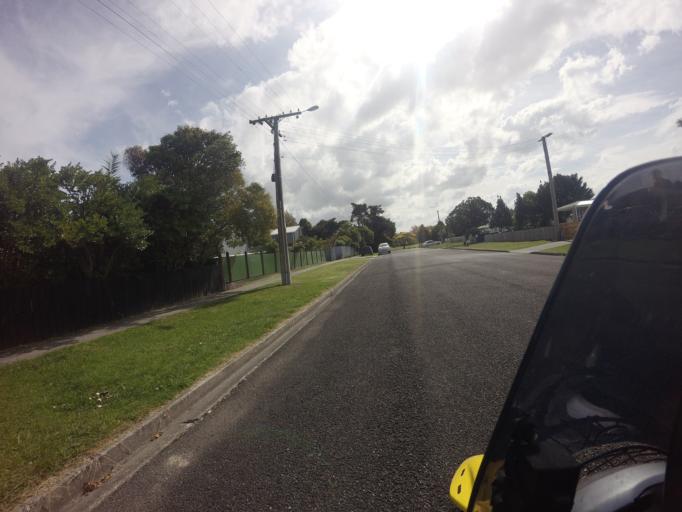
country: NZ
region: Gisborne
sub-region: Gisborne District
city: Gisborne
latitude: -38.6846
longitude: 178.0561
